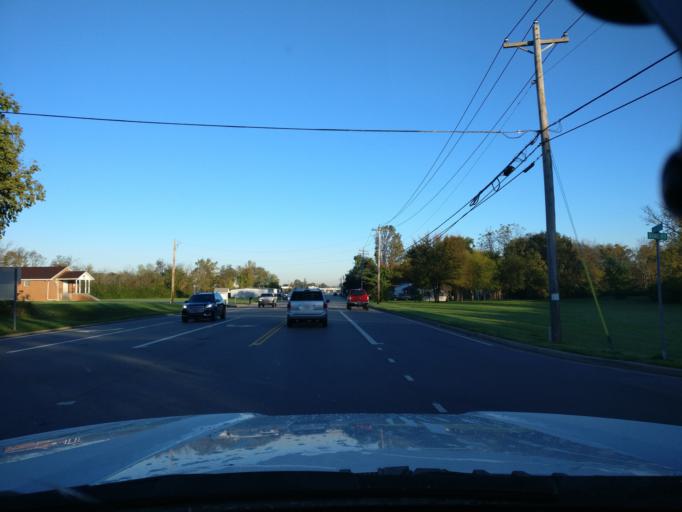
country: US
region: Ohio
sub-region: Warren County
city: Franklin
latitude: 39.5358
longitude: -84.2870
